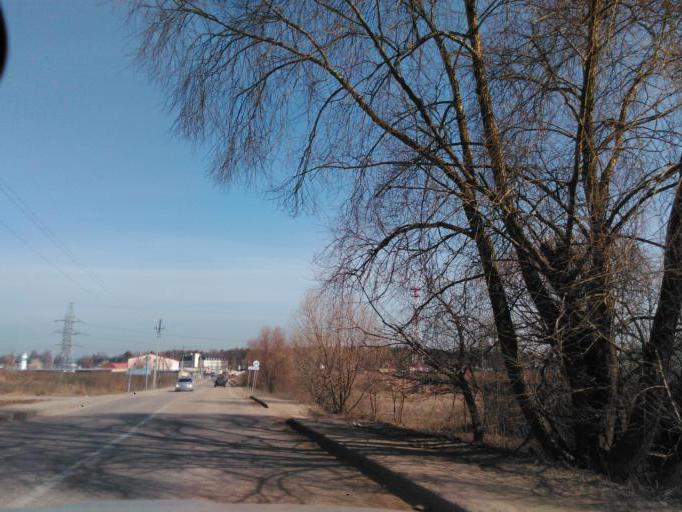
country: RU
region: Moskovskaya
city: Skhodnya
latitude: 55.8956
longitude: 37.2701
